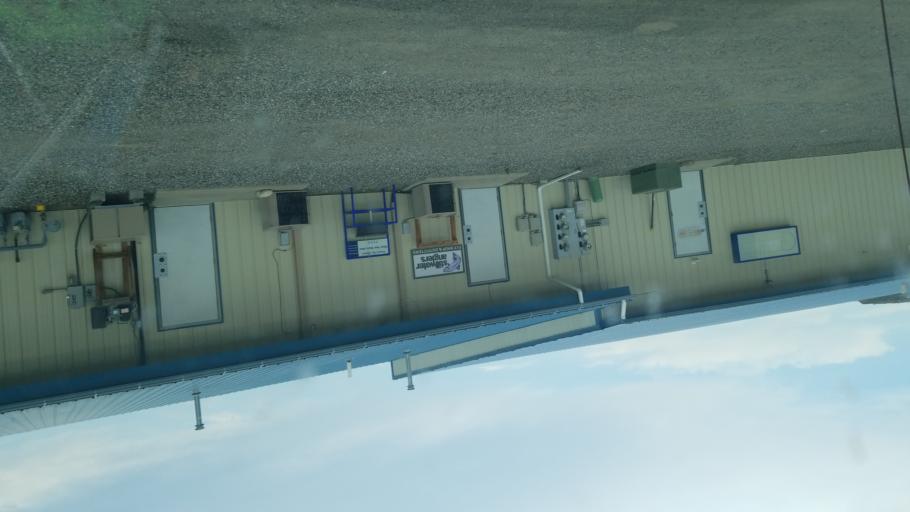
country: US
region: Montana
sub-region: Stillwater County
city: Columbus
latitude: 45.6425
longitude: -109.2483
